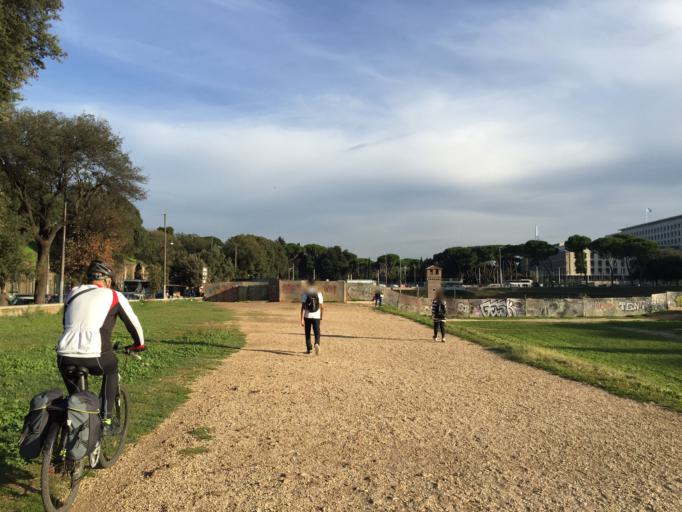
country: IT
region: Latium
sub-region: Citta metropolitana di Roma Capitale
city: Rome
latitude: 41.8861
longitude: 12.4867
